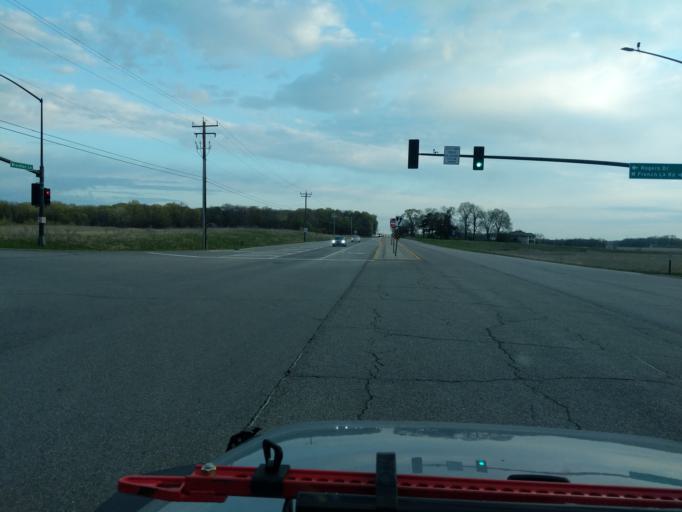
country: US
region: Minnesota
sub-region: Hennepin County
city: Rogers
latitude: 45.1828
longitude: -93.5236
